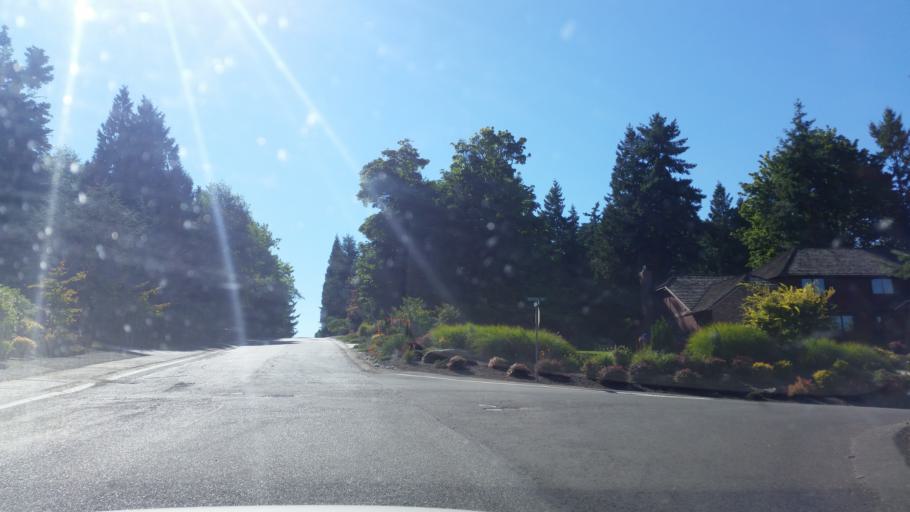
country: US
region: Washington
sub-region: Snohomish County
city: Woodway
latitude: 47.8003
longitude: -122.3864
